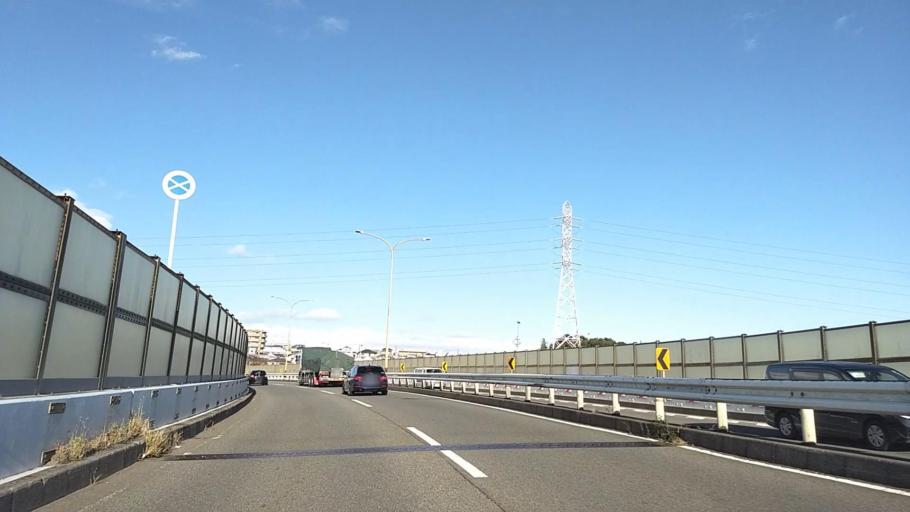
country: JP
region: Tokyo
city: Chofugaoka
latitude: 35.5824
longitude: 139.5973
